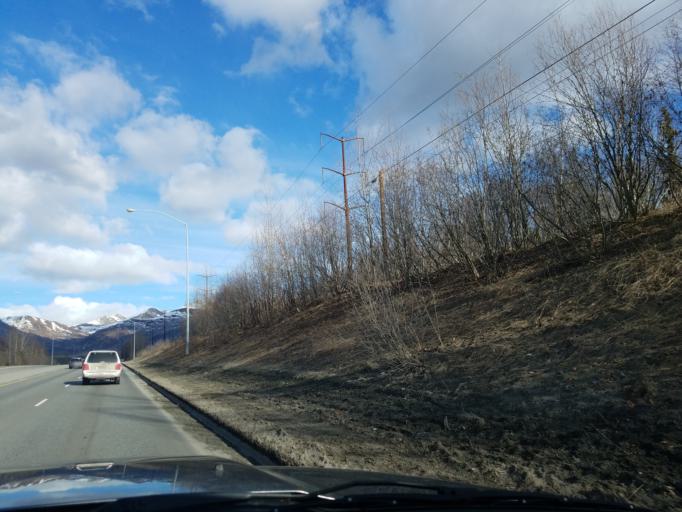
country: US
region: Alaska
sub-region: Anchorage Municipality
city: Anchorage
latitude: 61.1807
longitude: -149.7599
